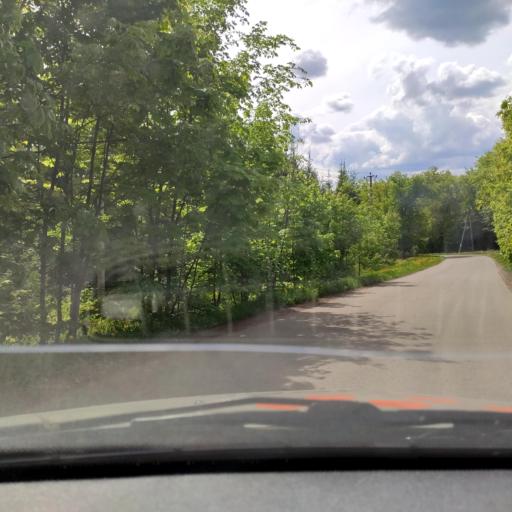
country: RU
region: Bashkortostan
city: Avdon
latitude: 54.6502
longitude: 55.7025
